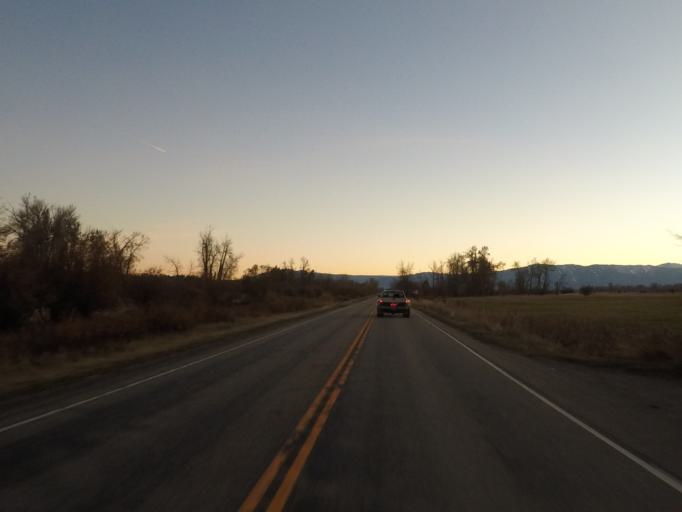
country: US
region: Montana
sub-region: Carbon County
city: Red Lodge
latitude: 45.3466
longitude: -109.1760
